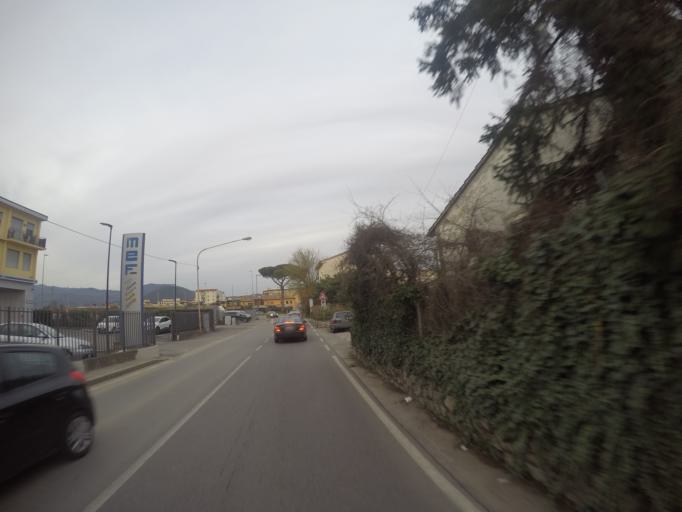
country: IT
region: Tuscany
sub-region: Provincia di Prato
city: Prato
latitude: 43.8832
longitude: 11.0682
